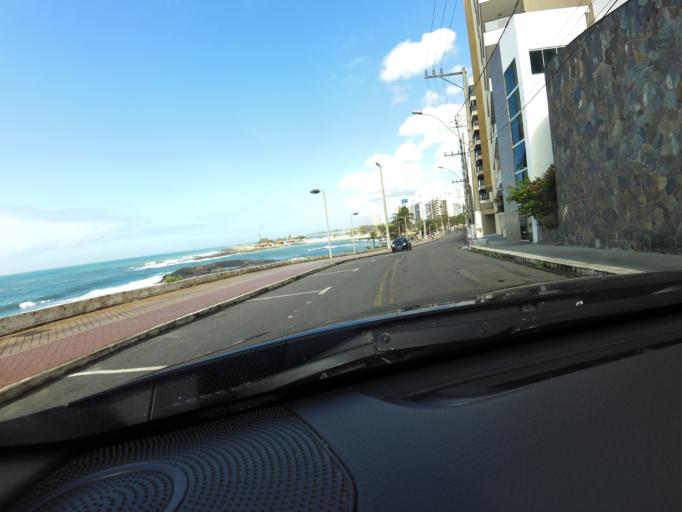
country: BR
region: Espirito Santo
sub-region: Guarapari
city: Guarapari
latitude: -20.6704
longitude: -40.4943
